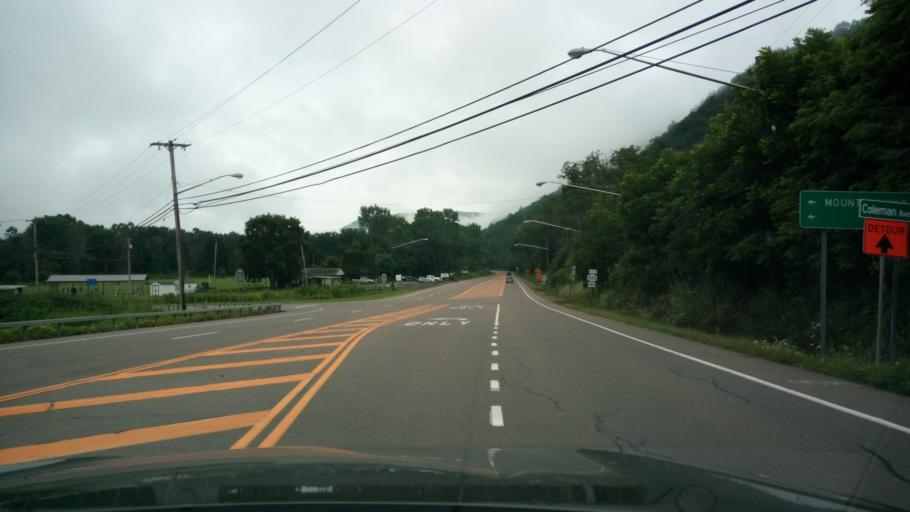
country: US
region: New York
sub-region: Chemung County
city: West Elmira
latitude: 42.0841
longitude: -76.8624
